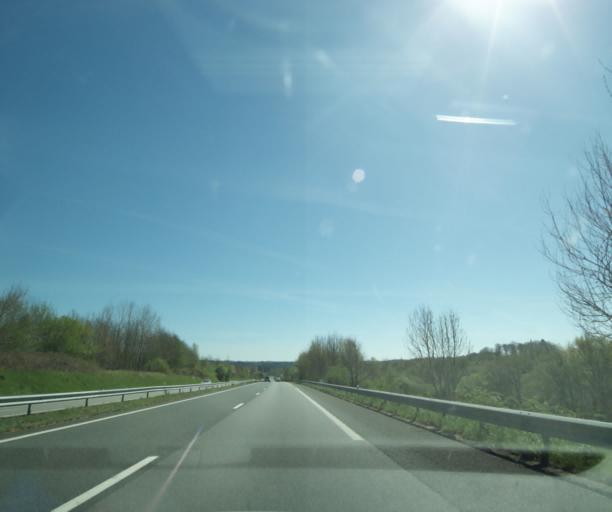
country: FR
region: Limousin
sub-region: Departement de la Correze
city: Vigeois
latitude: 45.4273
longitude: 1.5137
